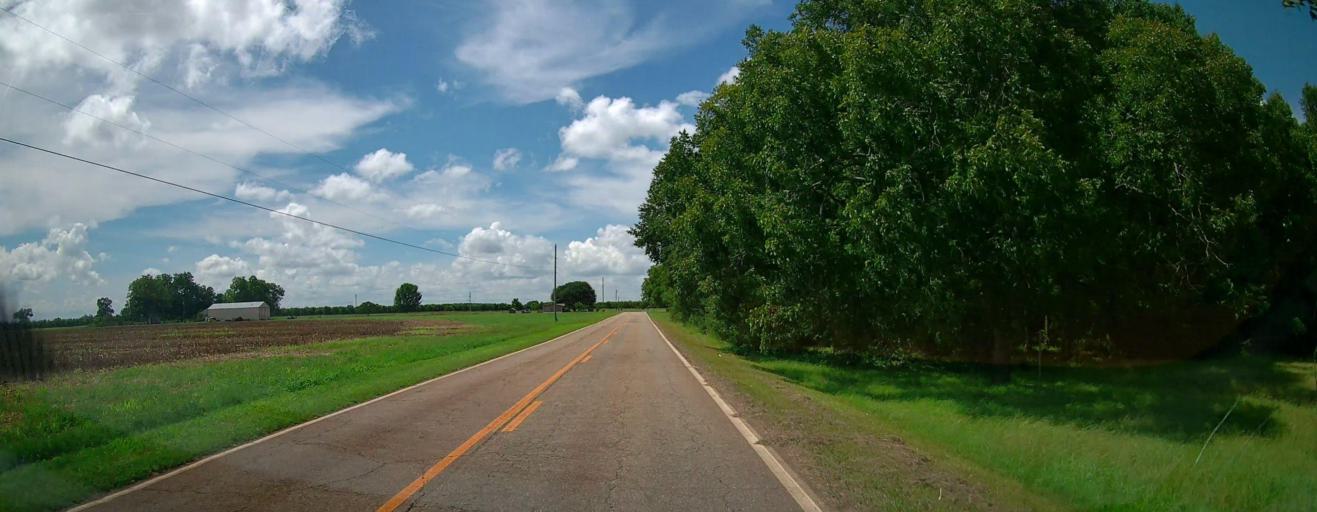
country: US
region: Georgia
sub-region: Peach County
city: Fort Valley
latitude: 32.5369
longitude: -83.8215
